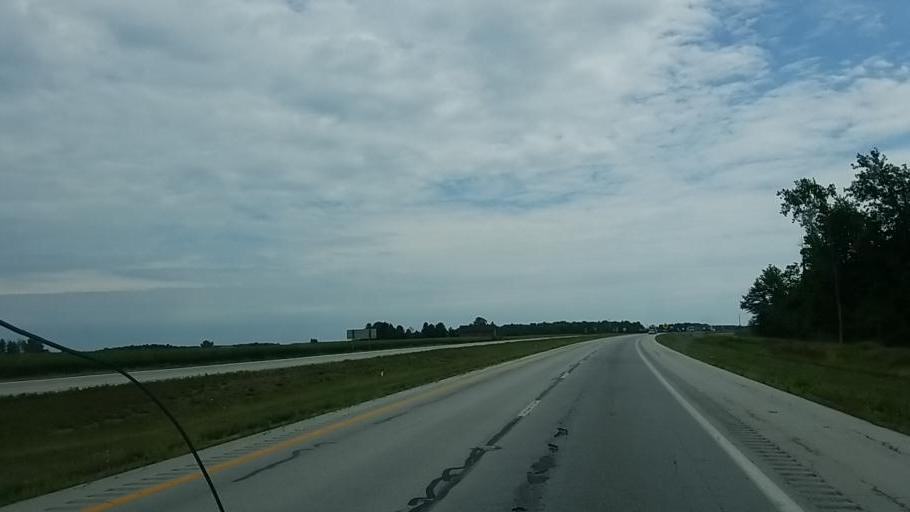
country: US
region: Ohio
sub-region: Hardin County
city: Forest
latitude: 40.8266
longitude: -83.4836
